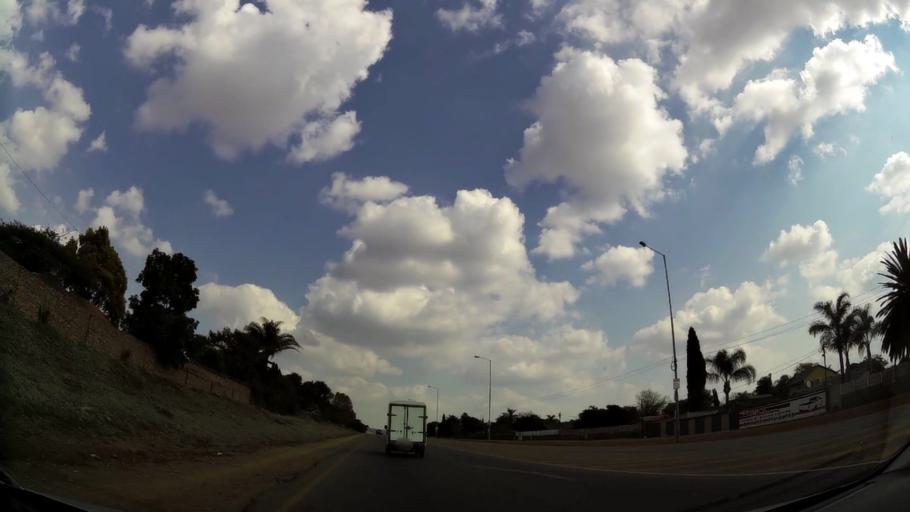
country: ZA
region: Gauteng
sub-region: City of Tshwane Metropolitan Municipality
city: Pretoria
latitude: -25.7988
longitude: 28.3160
